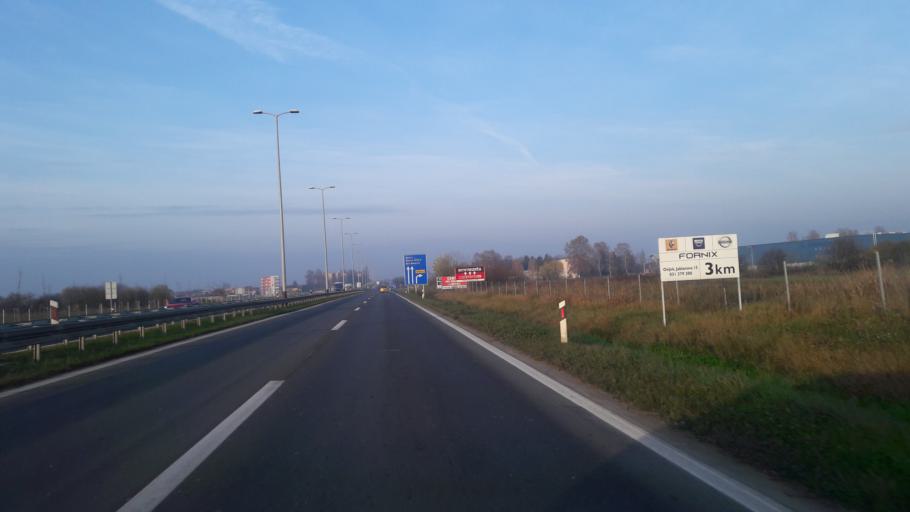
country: HR
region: Osjecko-Baranjska
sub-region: Grad Osijek
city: Osijek
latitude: 45.5418
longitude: 18.6842
